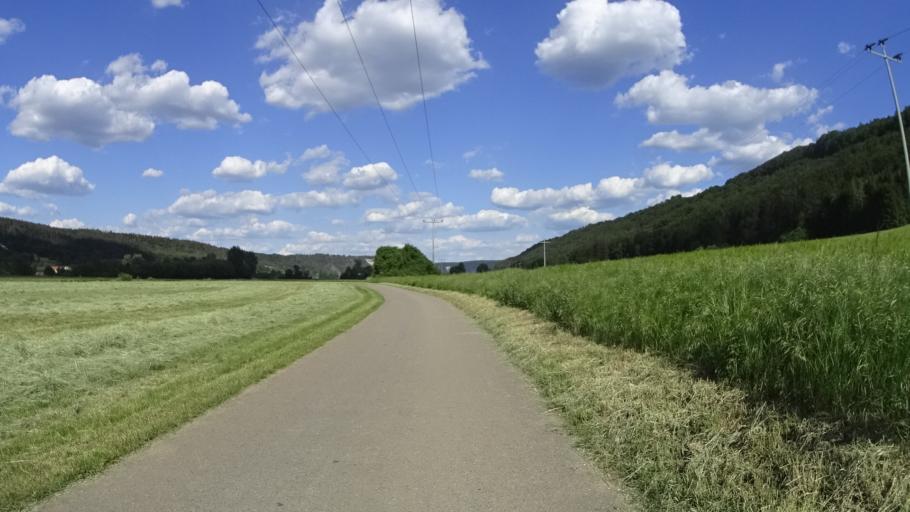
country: DE
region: Bavaria
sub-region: Upper Bavaria
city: Denkendorf
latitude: 49.0192
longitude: 11.4910
